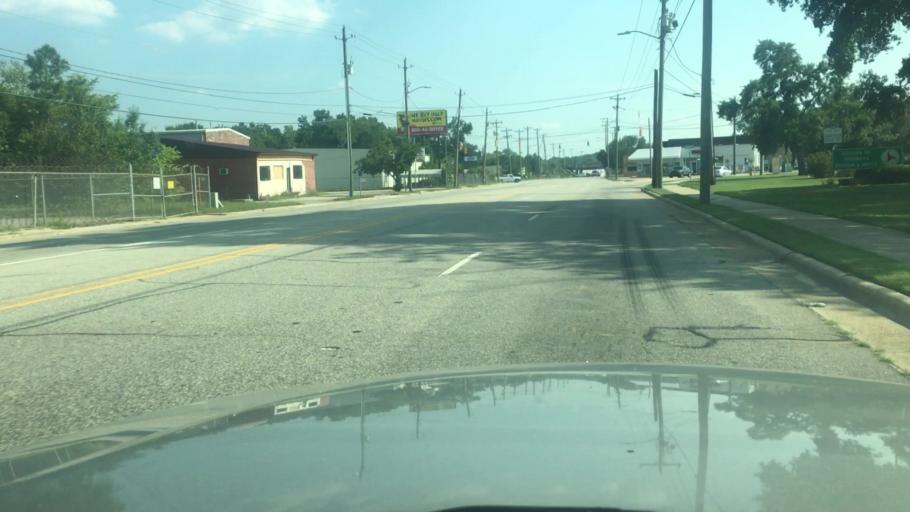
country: US
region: North Carolina
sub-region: Cumberland County
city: Fayetteville
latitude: 35.0429
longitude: -78.8817
